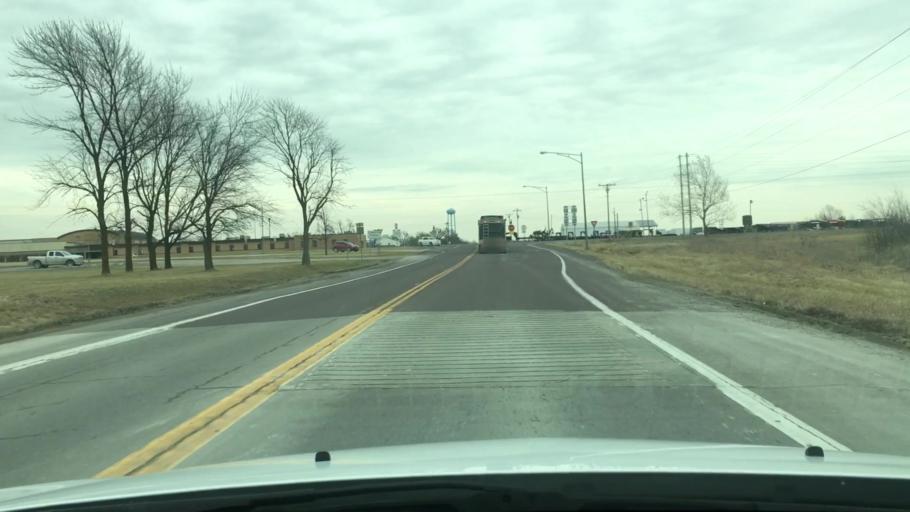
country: US
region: Missouri
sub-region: Montgomery County
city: Wellsville
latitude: 39.1630
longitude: -91.6500
